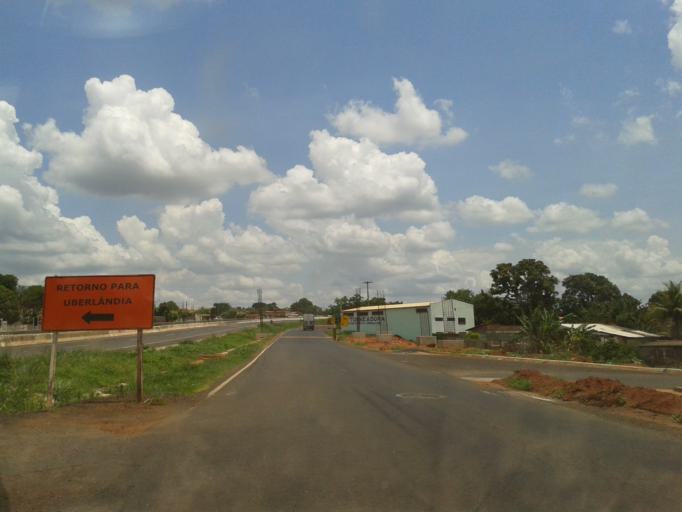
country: BR
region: Minas Gerais
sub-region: Monte Alegre De Minas
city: Monte Alegre de Minas
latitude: -18.8730
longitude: -48.8727
